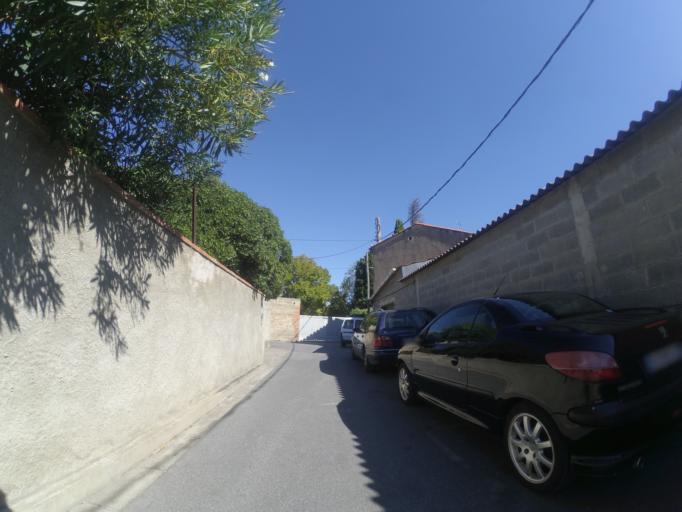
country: FR
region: Languedoc-Roussillon
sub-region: Departement des Pyrenees-Orientales
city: Baho
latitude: 42.6998
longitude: 2.8246
